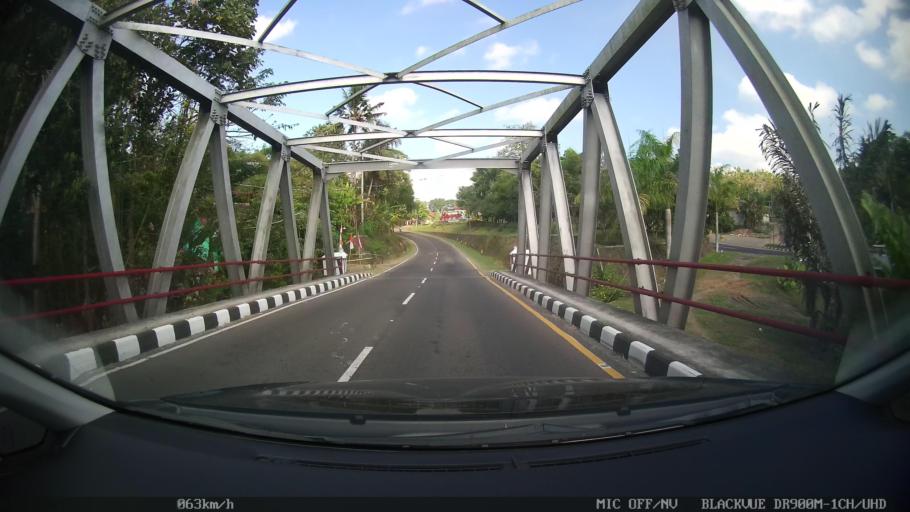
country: ID
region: Daerah Istimewa Yogyakarta
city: Godean
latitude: -7.8229
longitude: 110.2332
